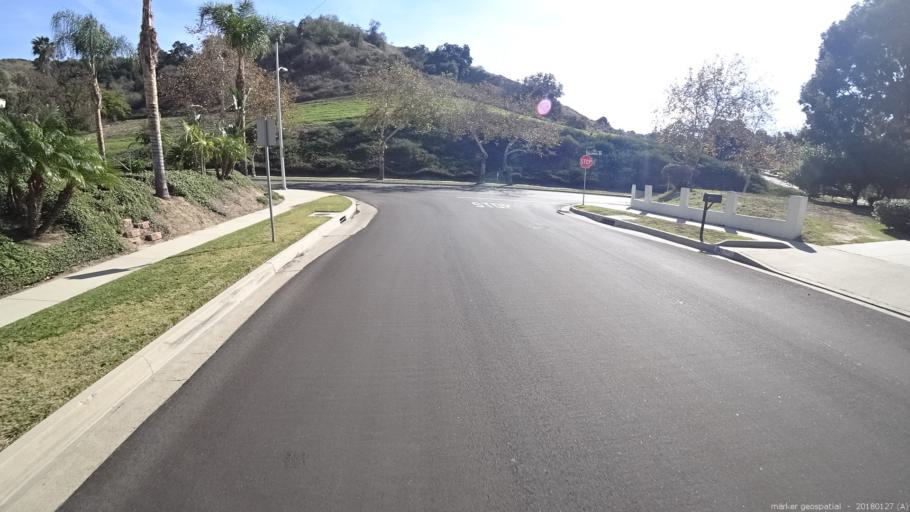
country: US
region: California
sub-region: Los Angeles County
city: Diamond Bar
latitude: 34.0144
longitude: -117.8058
